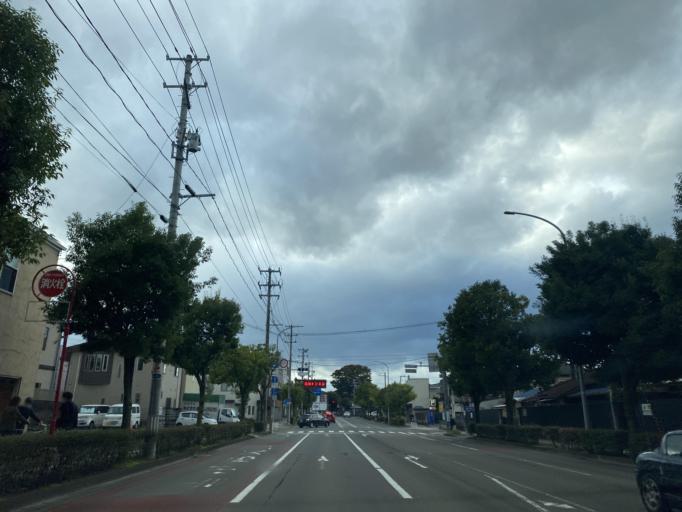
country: JP
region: Miyagi
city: Sendai-shi
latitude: 38.2786
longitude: 140.8627
